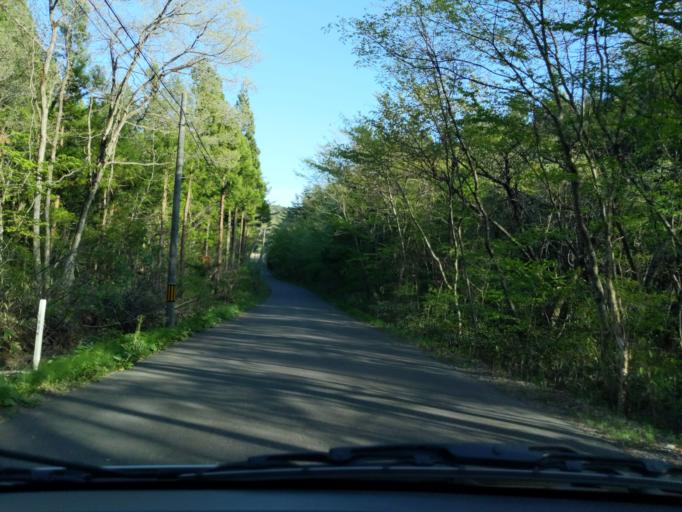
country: JP
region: Iwate
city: Ichinoseki
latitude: 38.8754
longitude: 140.9198
